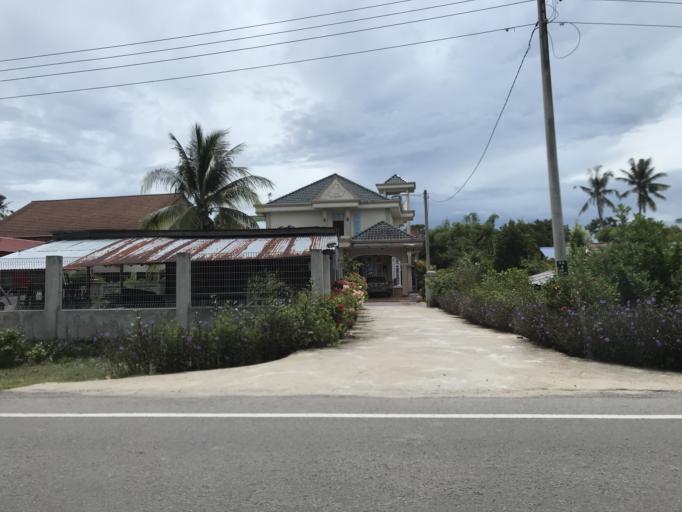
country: MY
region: Kelantan
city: Tumpat
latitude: 6.1759
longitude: 102.1964
